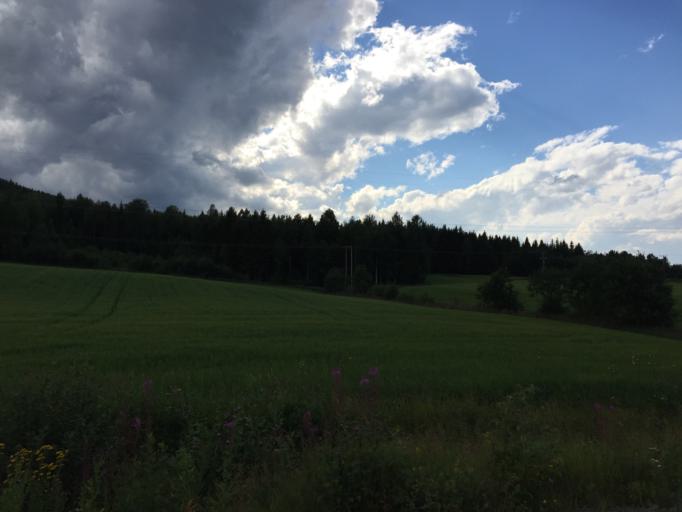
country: SE
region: Gaevleborg
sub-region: Ljusdals Kommun
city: Jaervsoe
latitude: 61.7437
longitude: 16.2713
